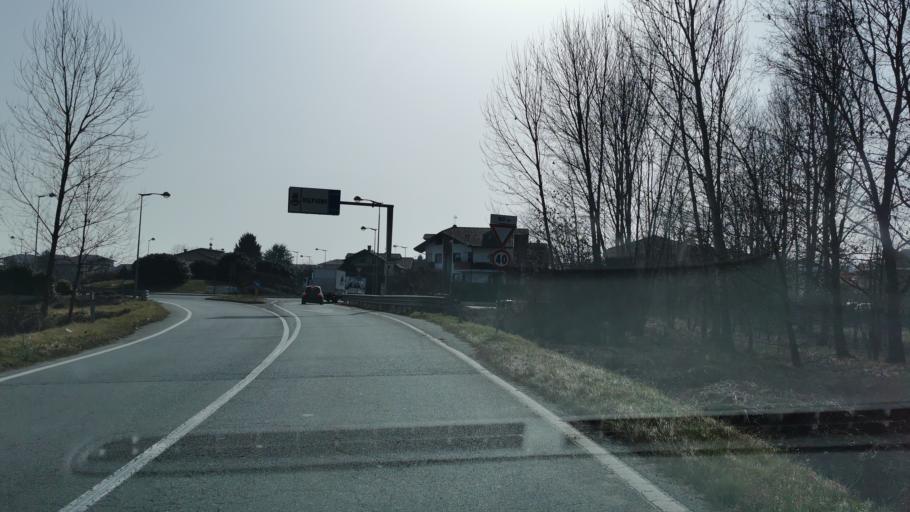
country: IT
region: Piedmont
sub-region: Provincia di Torino
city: Volpiano
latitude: 45.2111
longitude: 7.7732
